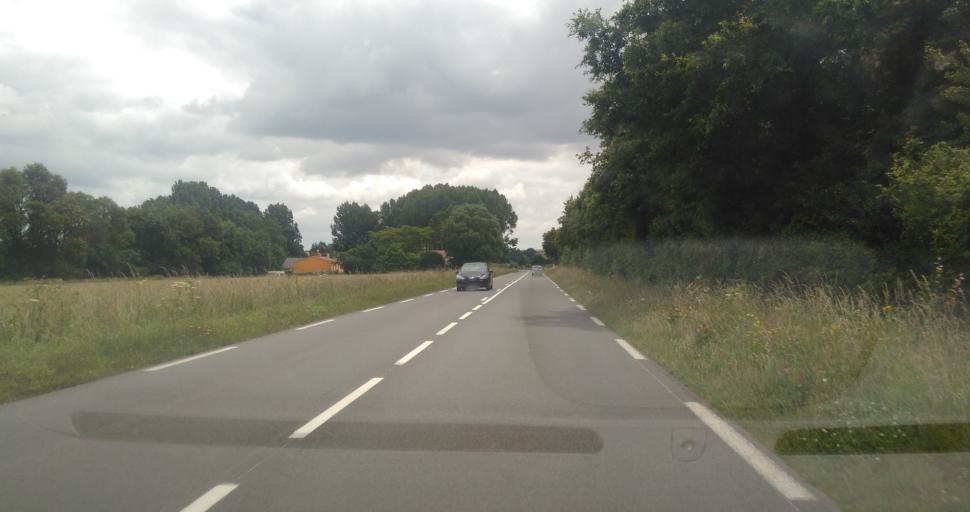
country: FR
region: Pays de la Loire
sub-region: Departement de la Vendee
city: Sainte-Hermine
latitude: 46.5808
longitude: -1.1104
